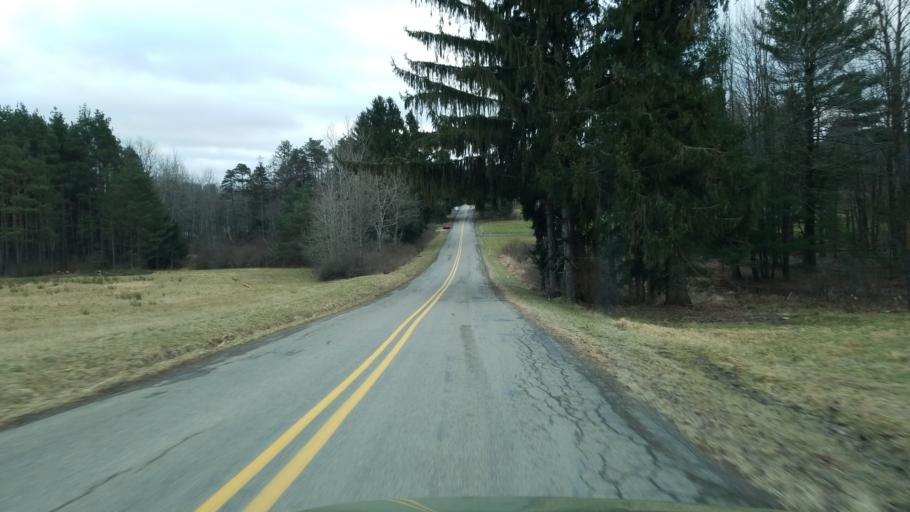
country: US
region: Pennsylvania
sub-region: Jefferson County
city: Falls Creek
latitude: 41.1698
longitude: -78.8121
